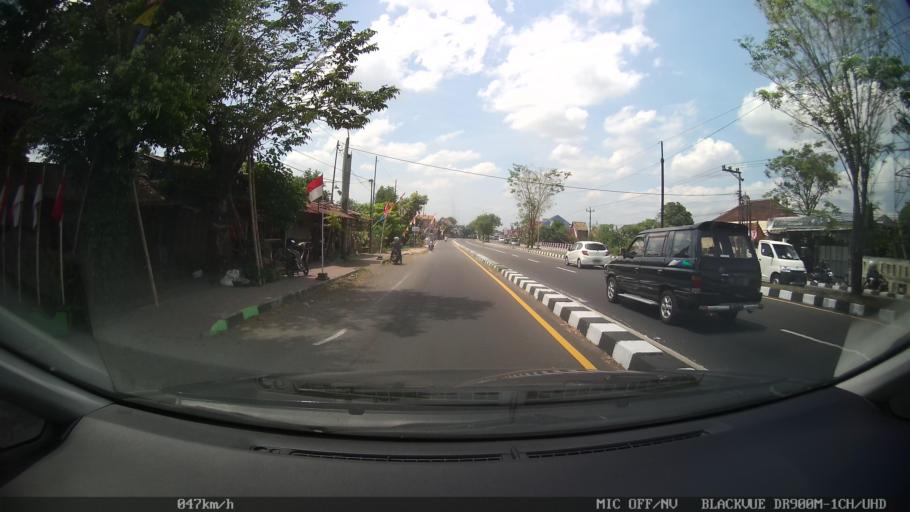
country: ID
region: Daerah Istimewa Yogyakarta
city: Kasihan
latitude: -7.8273
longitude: 110.3506
